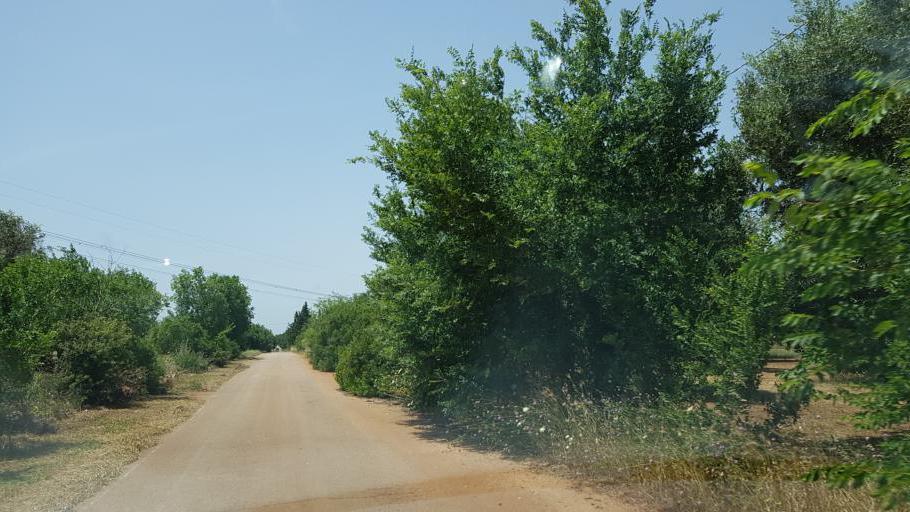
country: IT
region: Apulia
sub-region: Provincia di Lecce
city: Porto Cesareo
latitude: 40.3248
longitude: 17.8747
